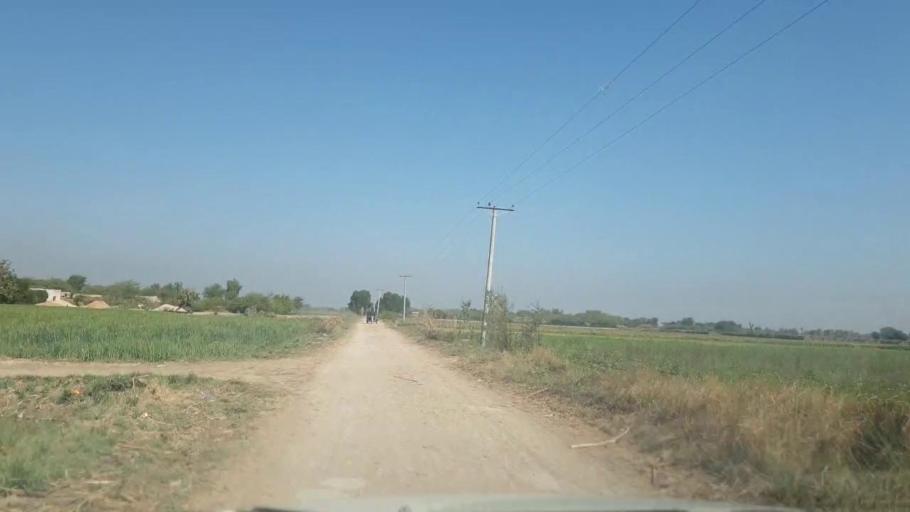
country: PK
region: Sindh
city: Mirpur Khas
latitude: 25.5058
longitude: 69.1582
